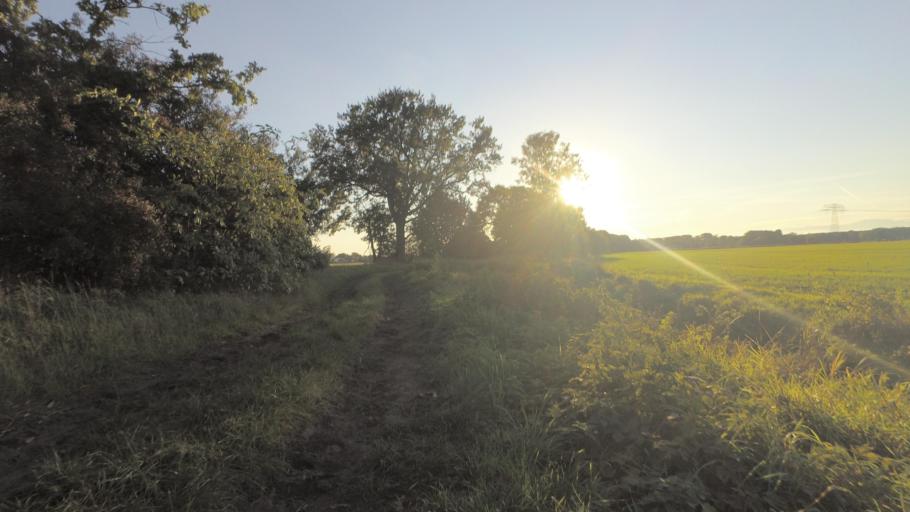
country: DE
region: Brandenburg
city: Ludwigsfelde
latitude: 52.2734
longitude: 13.3211
